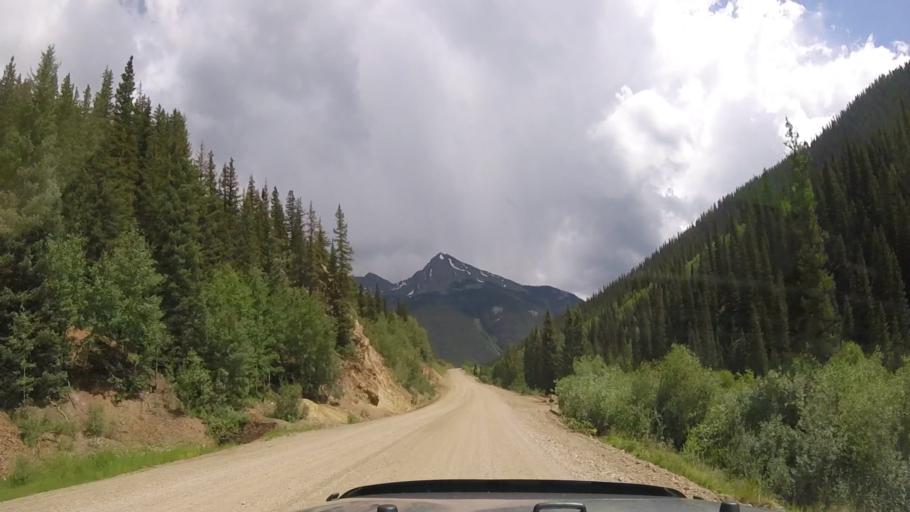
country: US
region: Colorado
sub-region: San Juan County
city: Silverton
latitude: 37.8260
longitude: -107.6677
